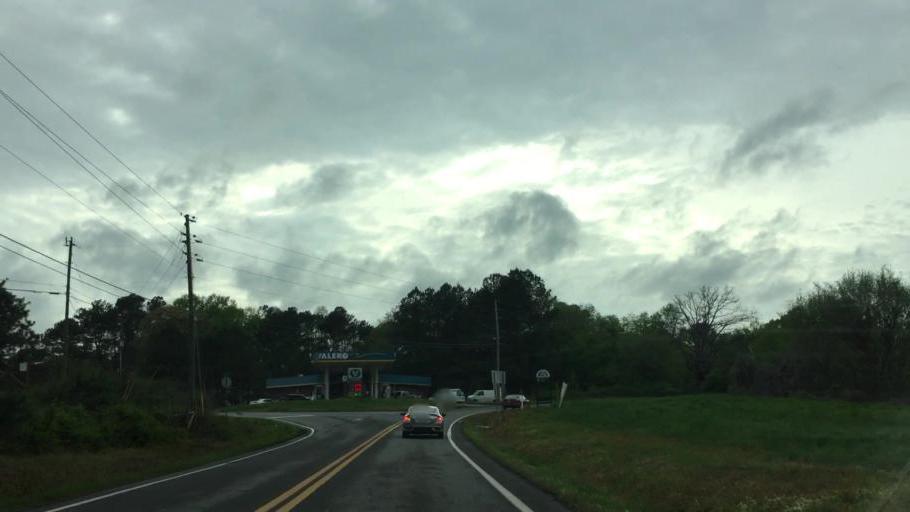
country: US
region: Georgia
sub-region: Fulton County
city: Milton
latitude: 34.1983
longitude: -84.3762
